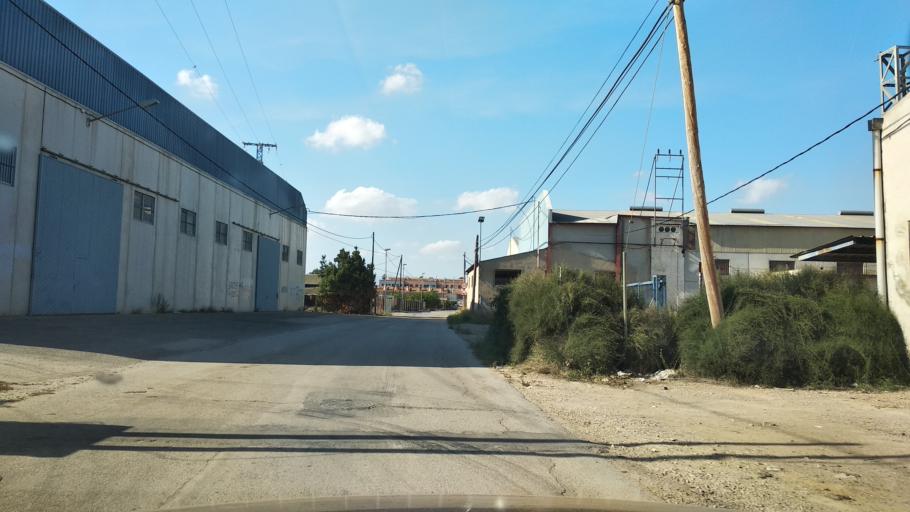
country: ES
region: Murcia
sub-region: Murcia
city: Santomera
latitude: 38.0558
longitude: -1.0431
